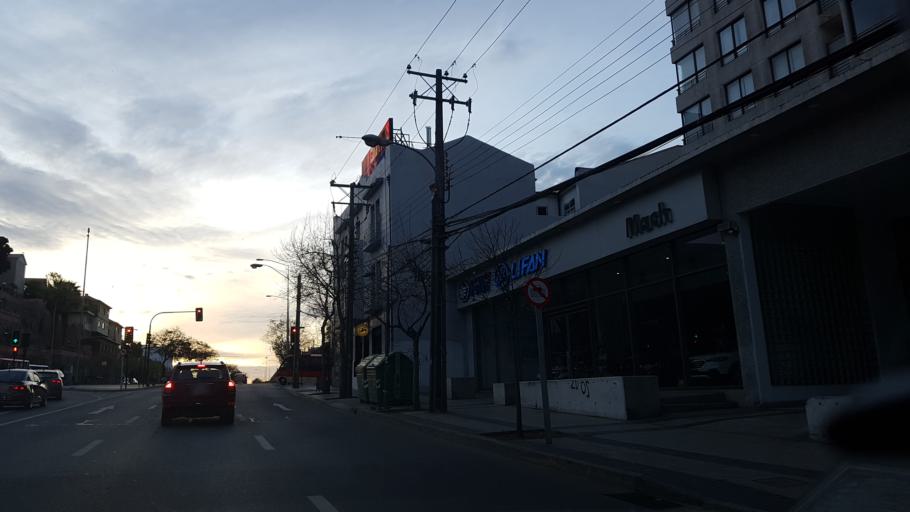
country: CL
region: Valparaiso
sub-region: Provincia de Valparaiso
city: Vina del Mar
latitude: -33.0248
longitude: -71.5618
